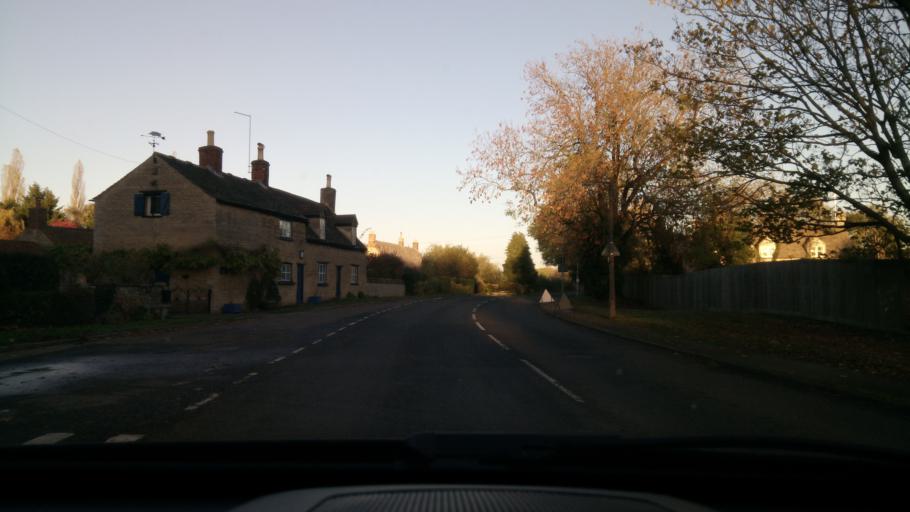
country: GB
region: England
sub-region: Peterborough
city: Ufford
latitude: 52.6412
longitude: -0.3827
